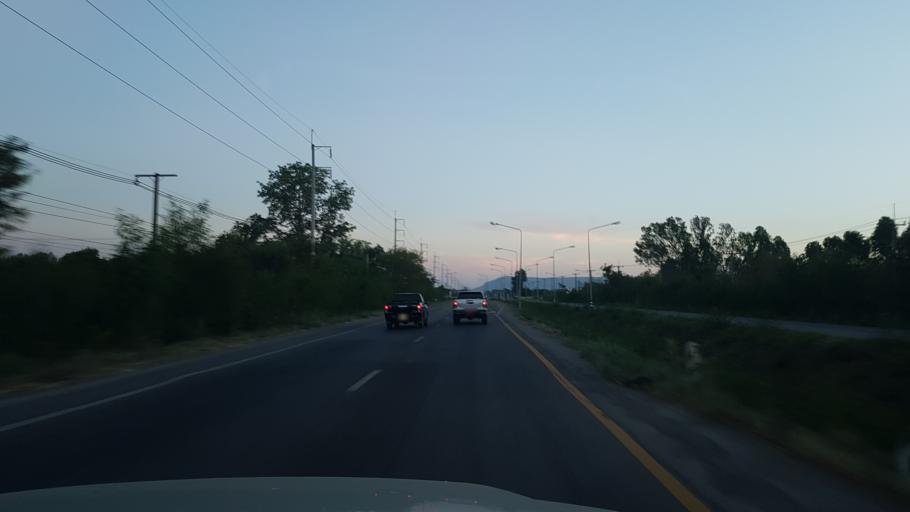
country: TH
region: Chaiyaphum
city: Phu Khiao
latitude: 16.4405
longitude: 102.1260
